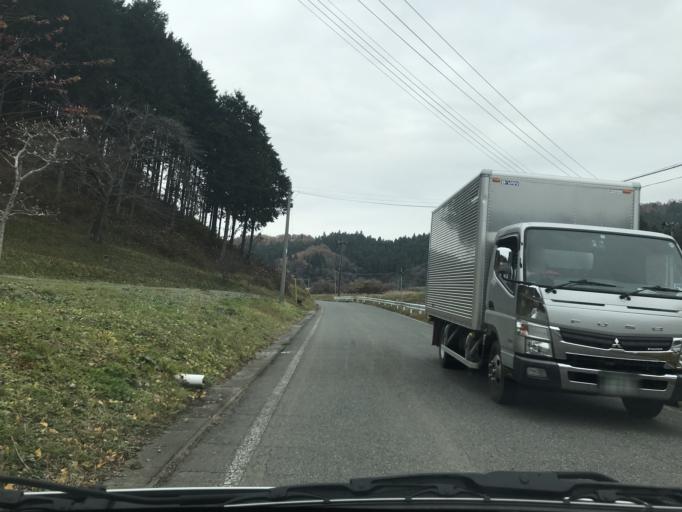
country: JP
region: Iwate
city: Kitakami
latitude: 39.2814
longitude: 141.1759
